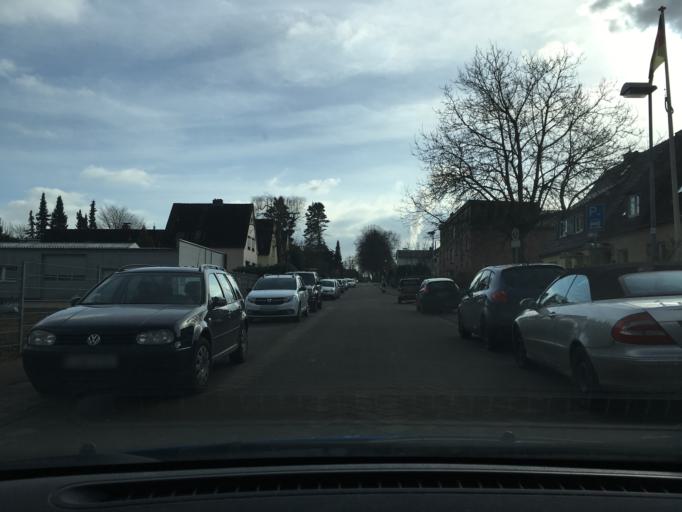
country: DE
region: Schleswig-Holstein
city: Wedel
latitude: 53.5848
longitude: 9.7210
